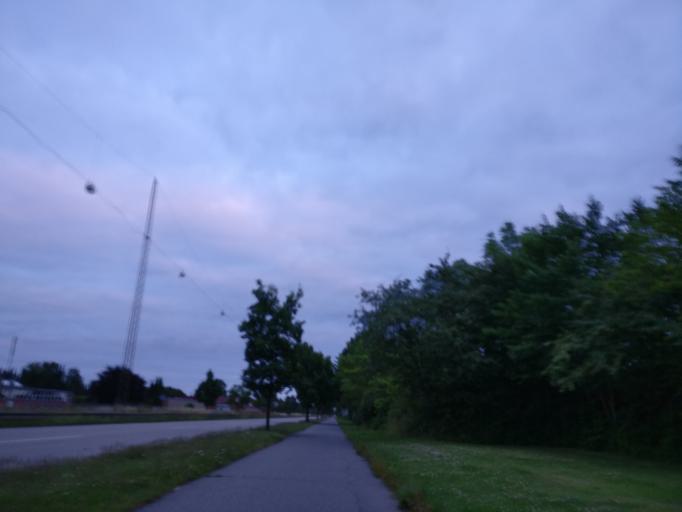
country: DK
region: Capital Region
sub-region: Hvidovre Kommune
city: Hvidovre
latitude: 55.6430
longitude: 12.4624
